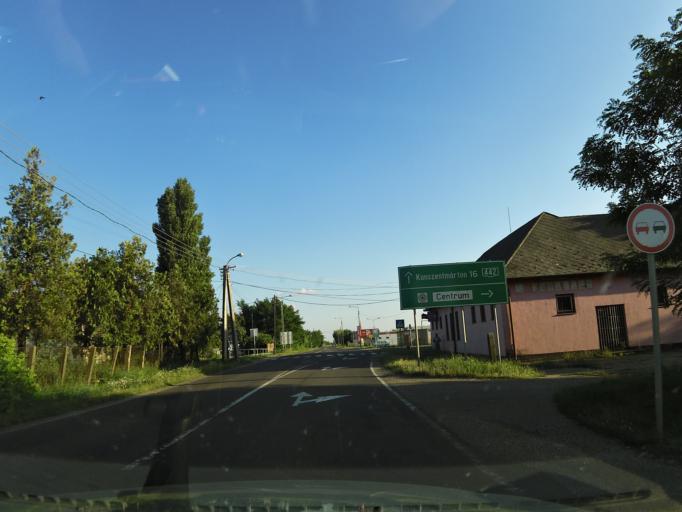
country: HU
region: Jasz-Nagykun-Szolnok
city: Tiszafoldvar
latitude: 46.9763
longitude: 20.2763
